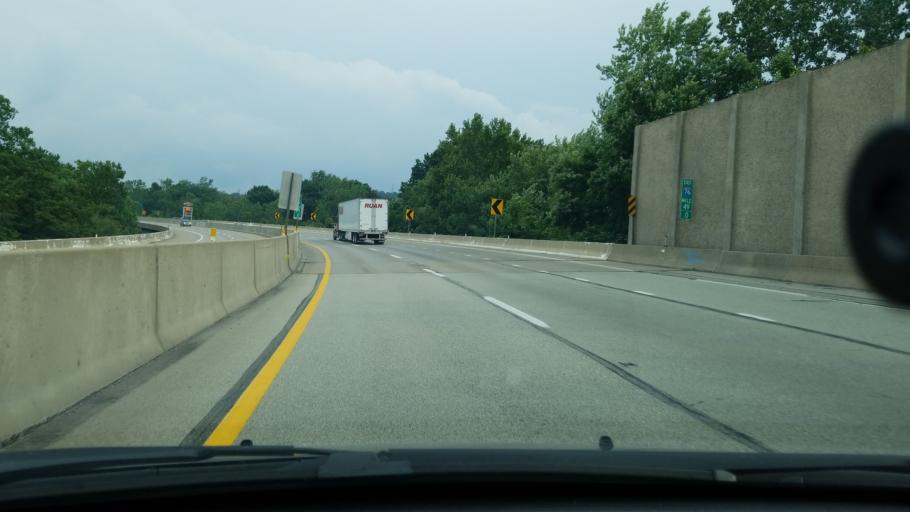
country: US
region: Pennsylvania
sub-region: Allegheny County
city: Oakmont
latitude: 40.5240
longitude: -79.8195
